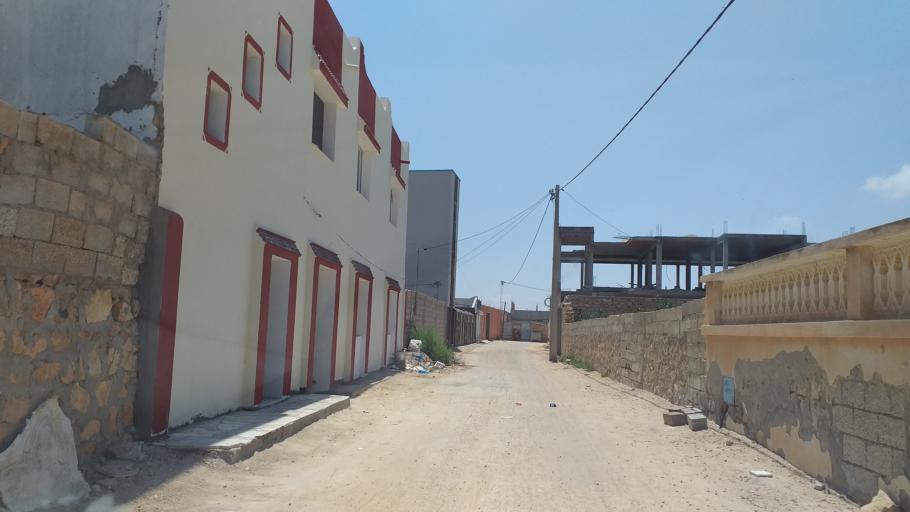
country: TN
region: Qabis
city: Gabes
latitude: 33.9451
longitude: 10.0574
